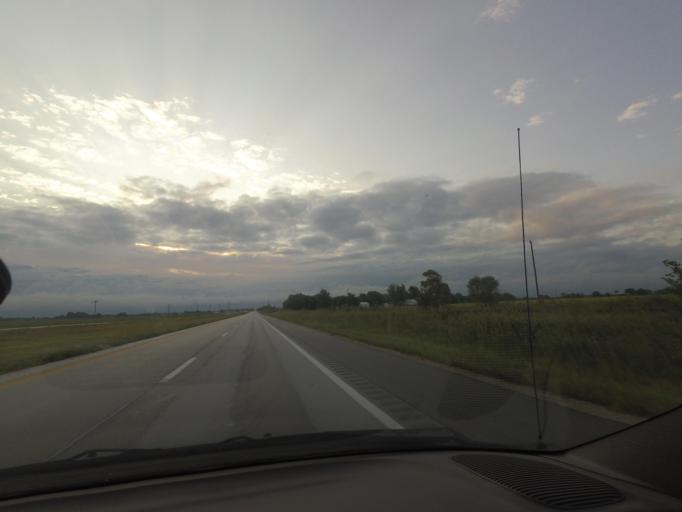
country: US
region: Missouri
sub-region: Shelby County
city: Shelbina
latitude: 39.7028
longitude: -92.0784
